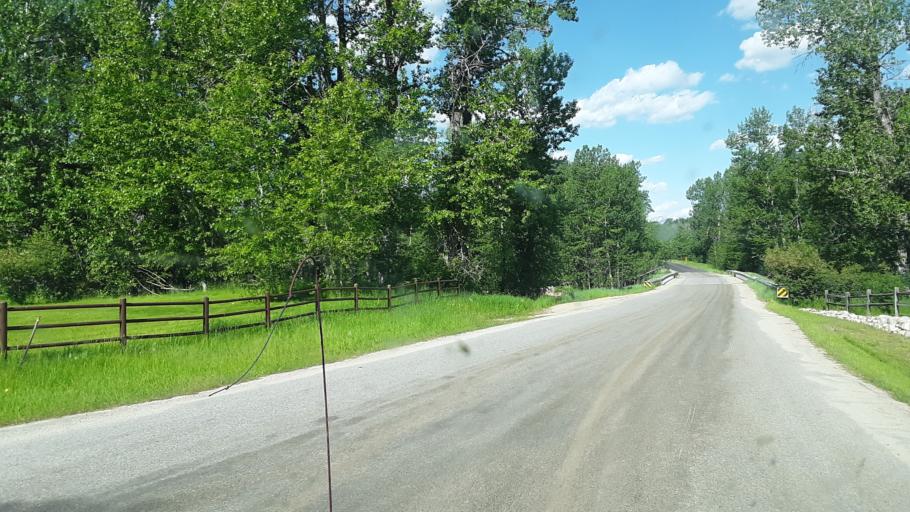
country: US
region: Montana
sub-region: Carbon County
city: Red Lodge
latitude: 45.2772
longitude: -109.2085
